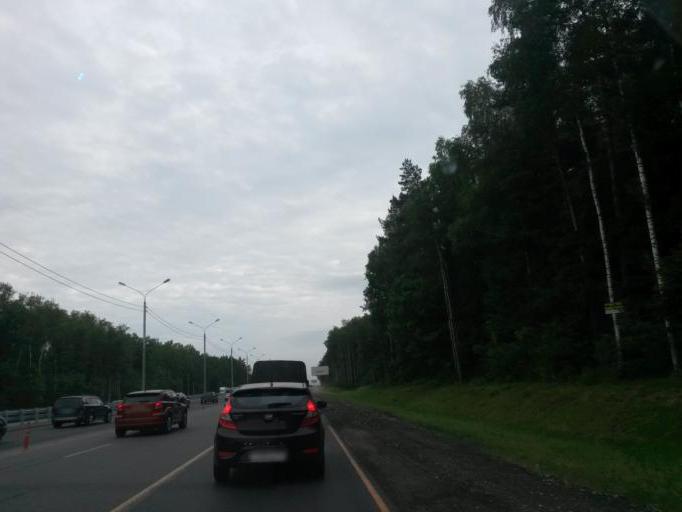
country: RU
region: Moskovskaya
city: Lyubuchany
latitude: 55.2643
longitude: 37.5348
